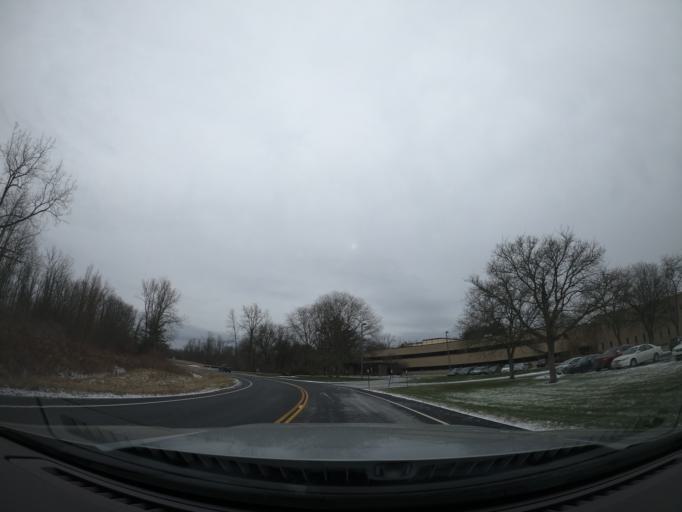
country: US
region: New York
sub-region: Tompkins County
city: Northeast Ithaca
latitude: 42.4857
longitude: -76.4576
